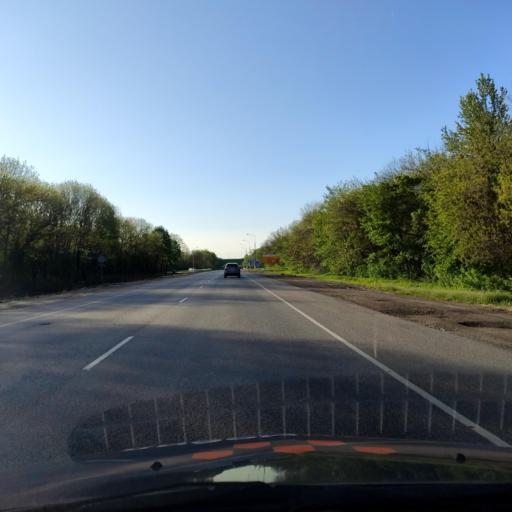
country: RU
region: Lipetsk
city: Yelets
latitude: 52.5499
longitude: 38.7112
